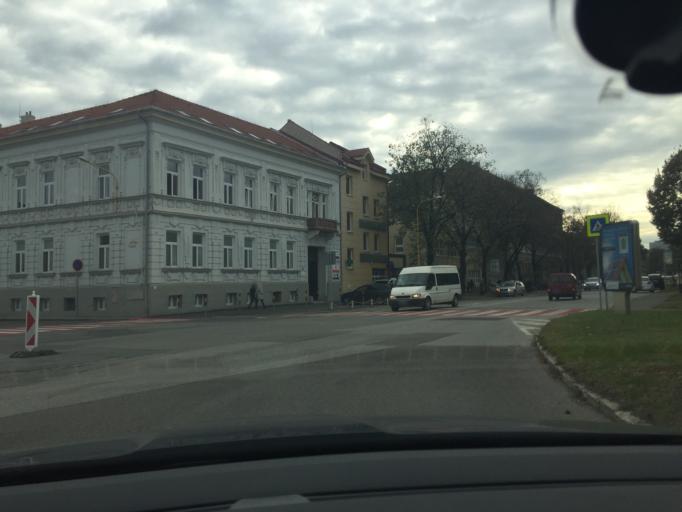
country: SK
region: Kosicky
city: Kosice
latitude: 48.7287
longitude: 21.2605
